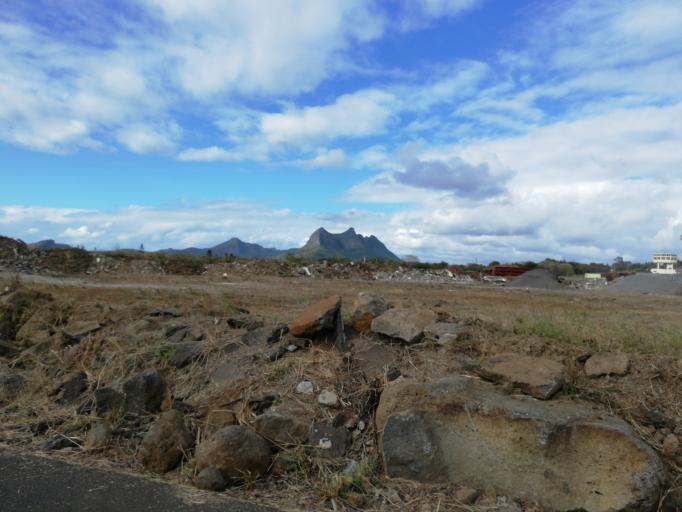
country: MU
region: Black River
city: Gros Cailloux
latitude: -20.2272
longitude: 57.4517
